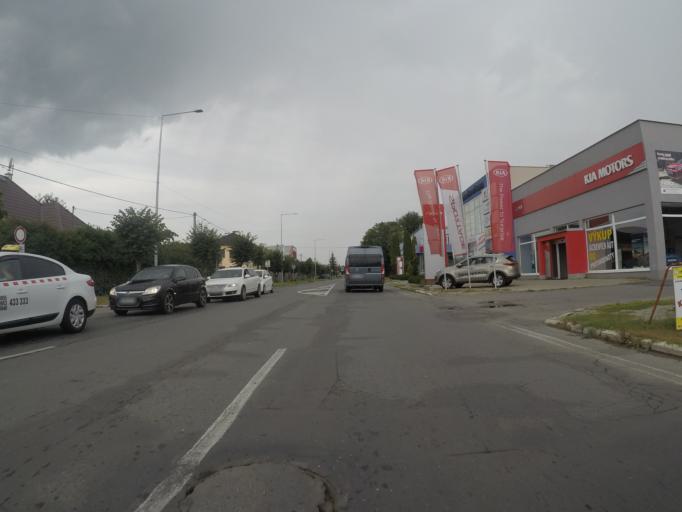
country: SK
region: Kosicky
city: Spisska Nova Ves
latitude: 48.9490
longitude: 20.5531
